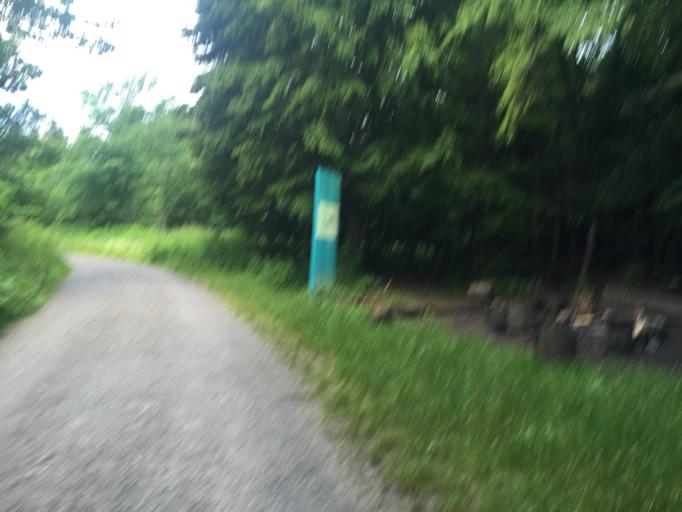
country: CH
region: Bern
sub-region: Bern-Mittelland District
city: Koniz
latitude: 46.9367
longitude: 7.4092
